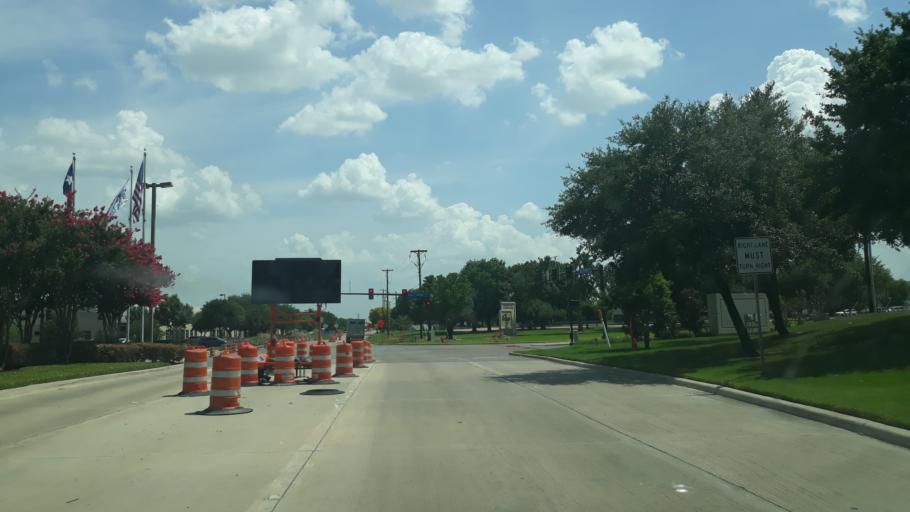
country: US
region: Texas
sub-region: Dallas County
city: Coppell
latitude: 32.9553
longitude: -97.0109
